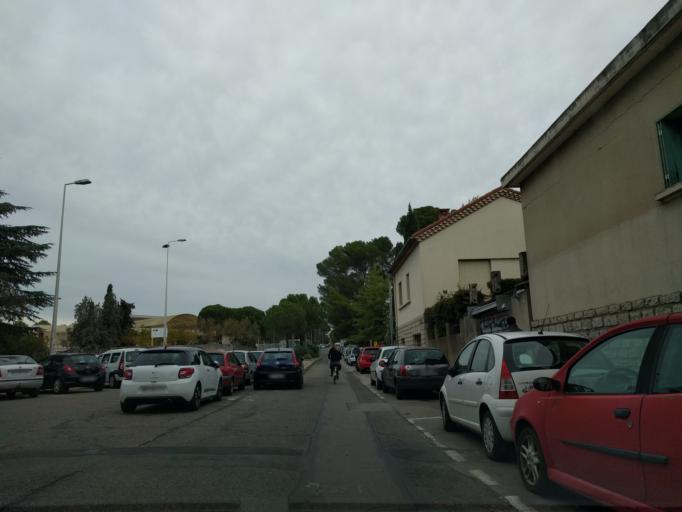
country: FR
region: Languedoc-Roussillon
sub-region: Departement de l'Herault
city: Montpellier
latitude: 43.6301
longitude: 3.8705
